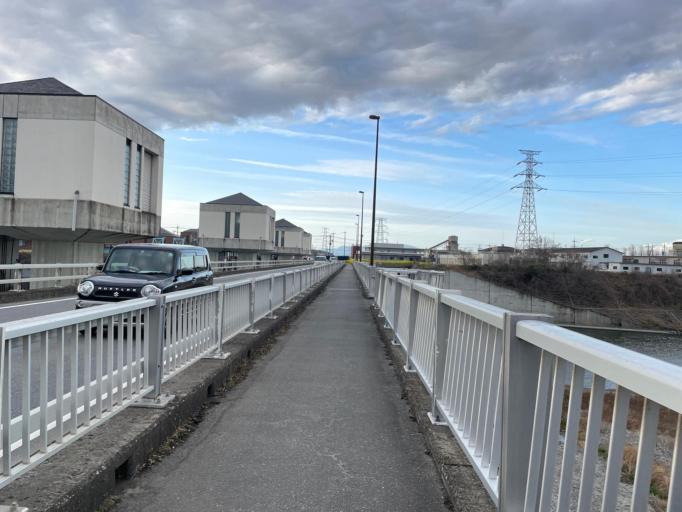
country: JP
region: Saitama
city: Fukayacho
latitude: 36.1328
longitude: 139.2662
